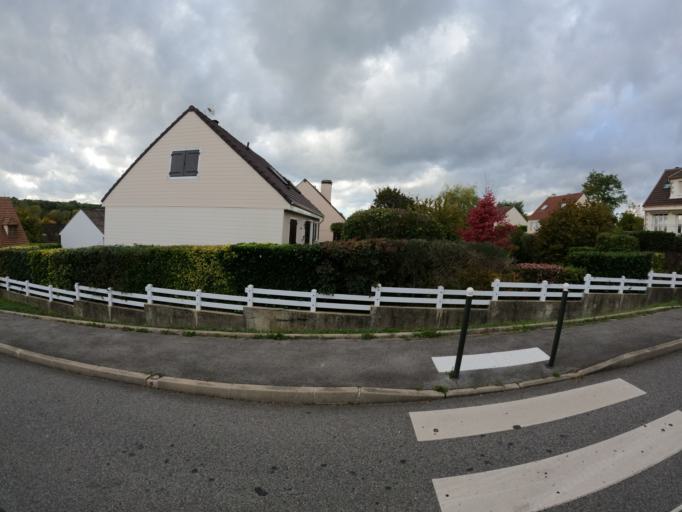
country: FR
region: Ile-de-France
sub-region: Departement de Seine-et-Marne
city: Coupvray
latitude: 48.8990
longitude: 2.7923
